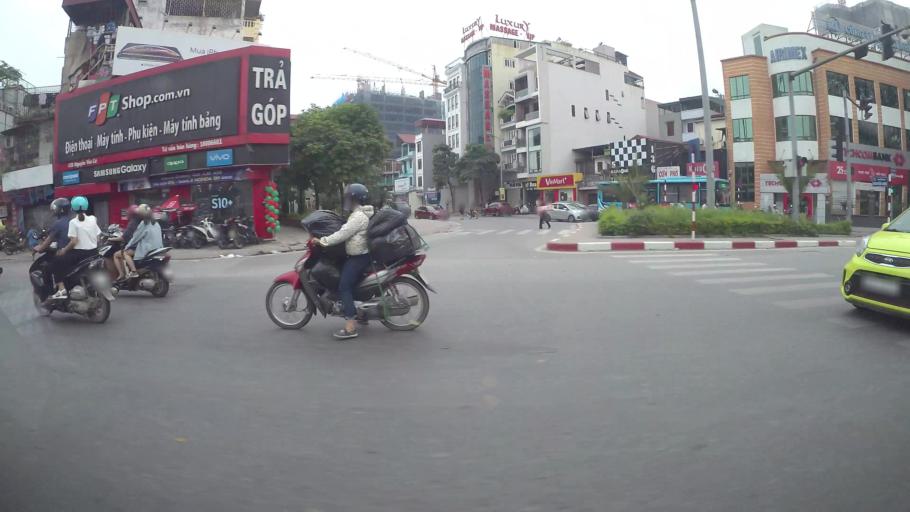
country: VN
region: Ha Noi
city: Hoan Kiem
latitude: 21.0463
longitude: 105.8777
